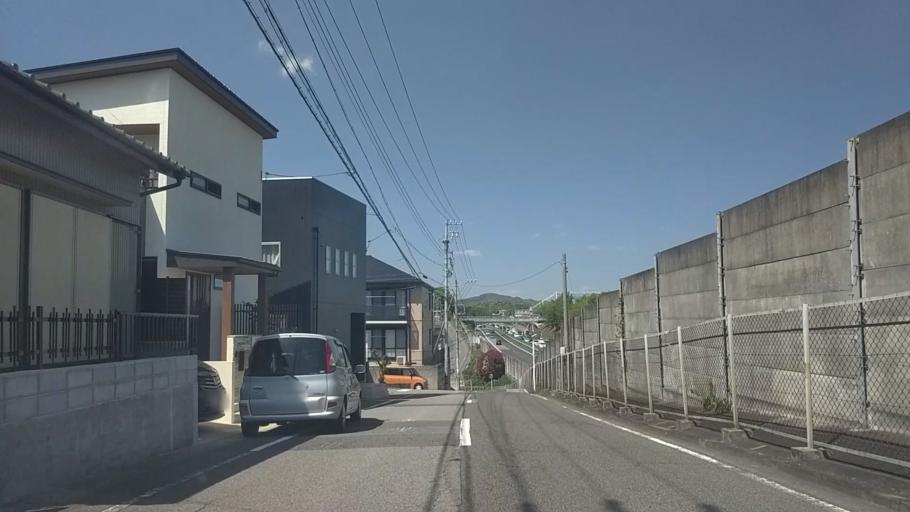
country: JP
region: Aichi
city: Okazaki
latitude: 34.9770
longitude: 137.1833
